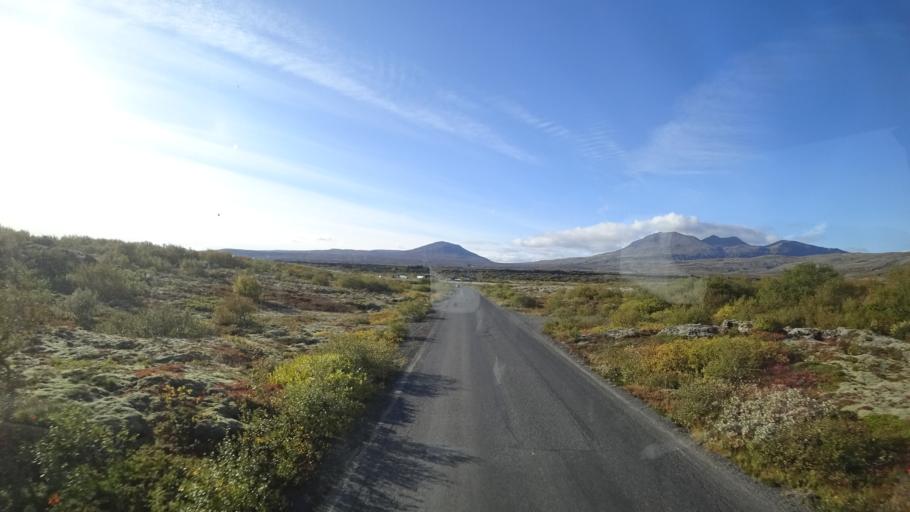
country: IS
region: South
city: Hveragerdi
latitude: 64.2784
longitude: -21.0804
